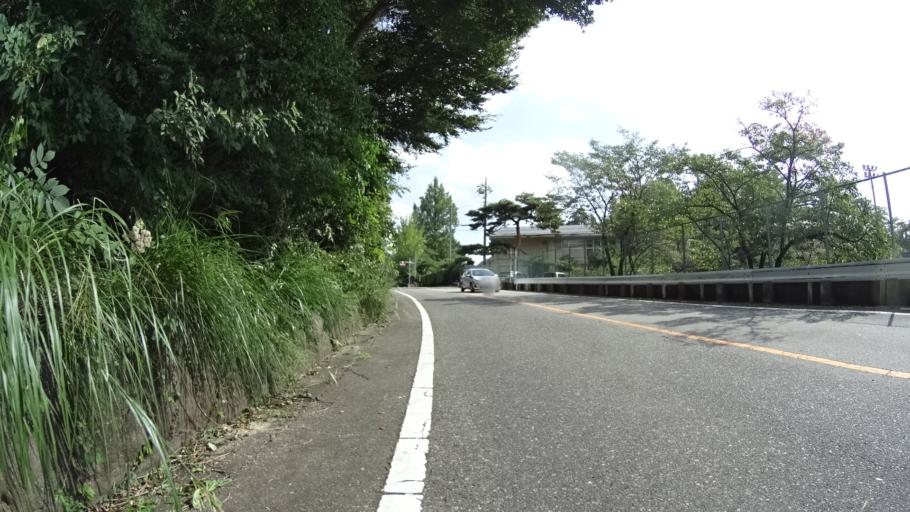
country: JP
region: Yamanashi
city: Kofu-shi
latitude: 35.7130
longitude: 138.5531
